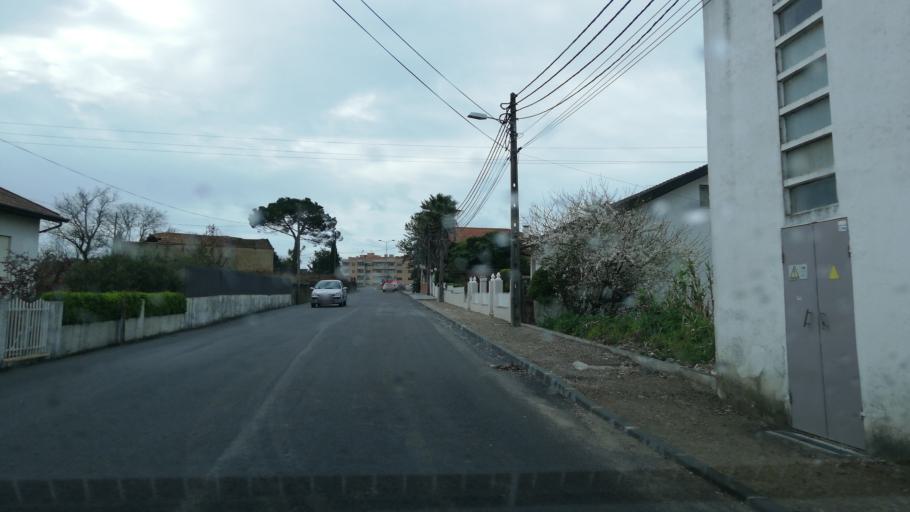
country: PT
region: Aveiro
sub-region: Agueda
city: Agueda
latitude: 40.5924
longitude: -8.4523
